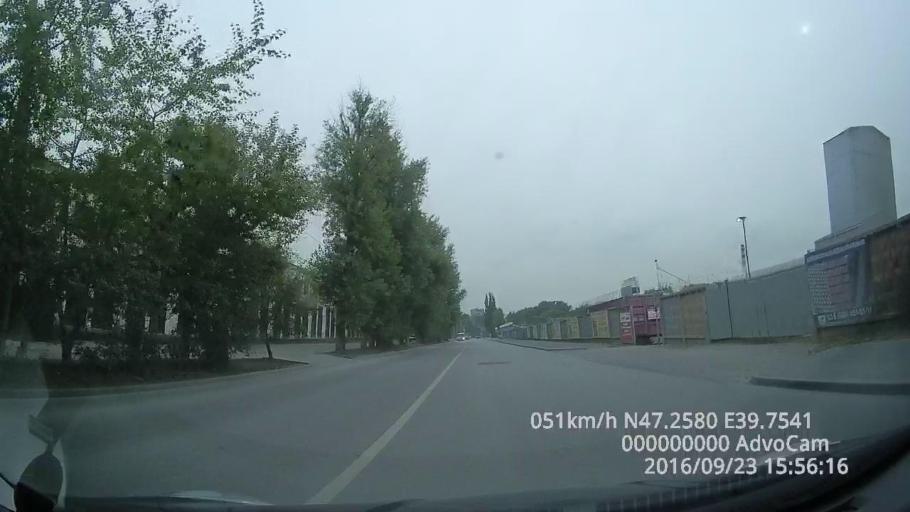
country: RU
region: Rostov
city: Imeni Chkalova
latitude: 47.2579
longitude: 39.7541
